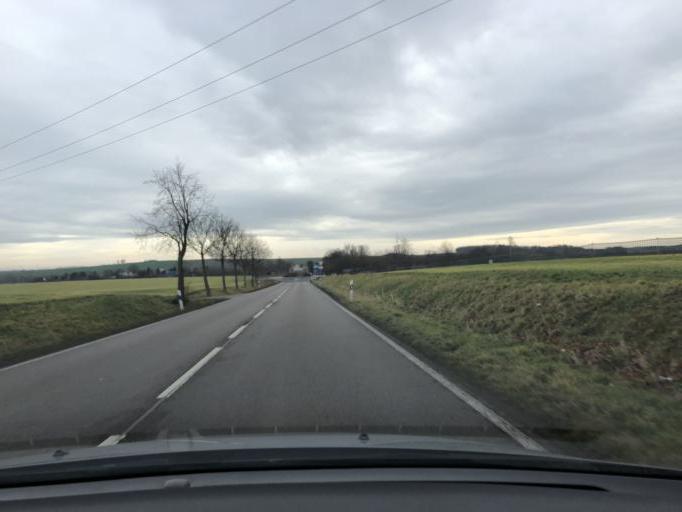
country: DE
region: Saxony
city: Nossen
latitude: 51.0613
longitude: 13.3420
